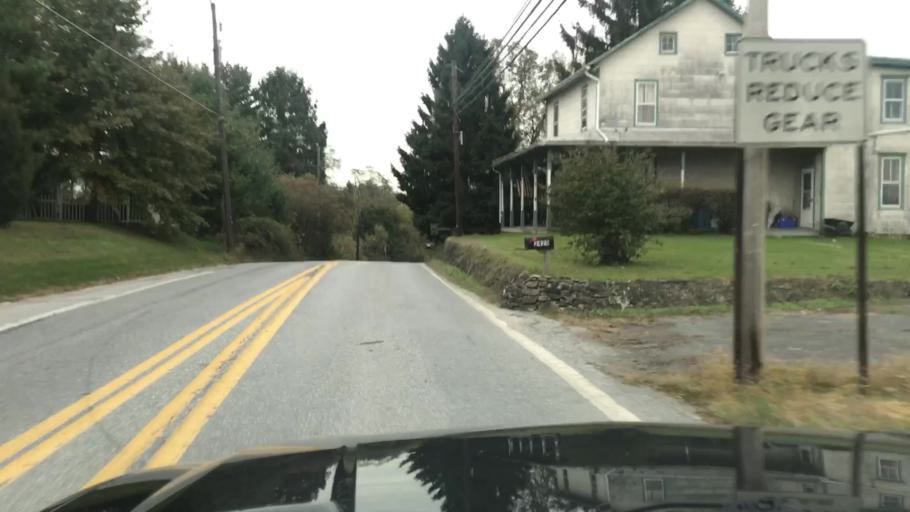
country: US
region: Pennsylvania
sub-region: Cumberland County
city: Mechanicsburg
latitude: 40.1706
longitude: -76.9799
